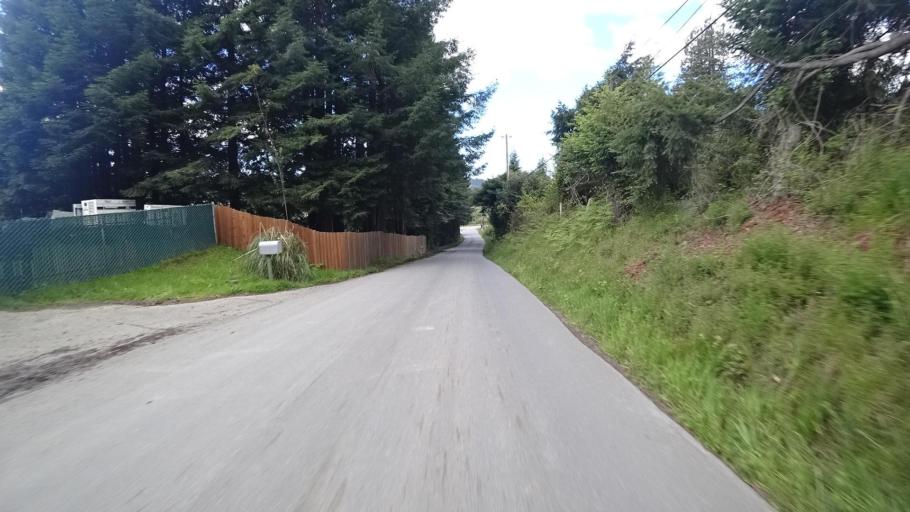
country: US
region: California
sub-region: Humboldt County
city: Blue Lake
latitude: 40.8975
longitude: -124.0055
